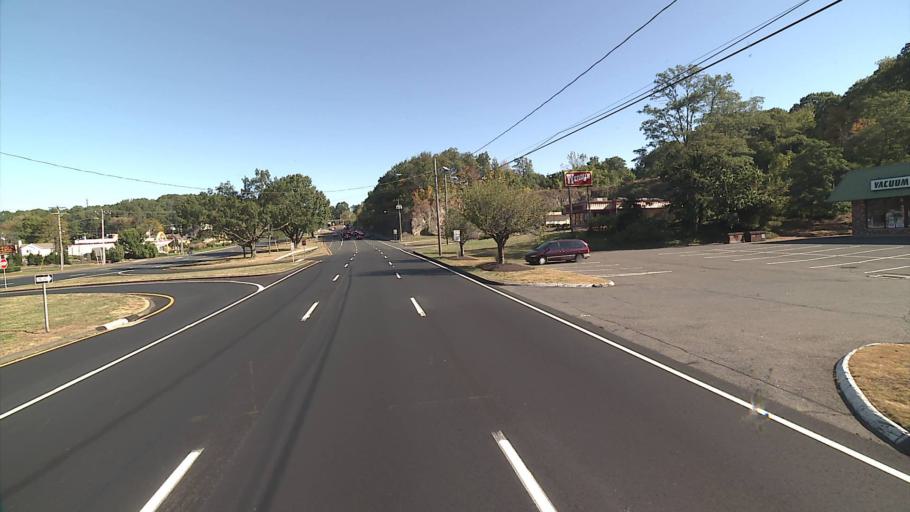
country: US
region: Connecticut
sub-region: Hartford County
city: Newington
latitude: 41.6861
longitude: -72.7081
